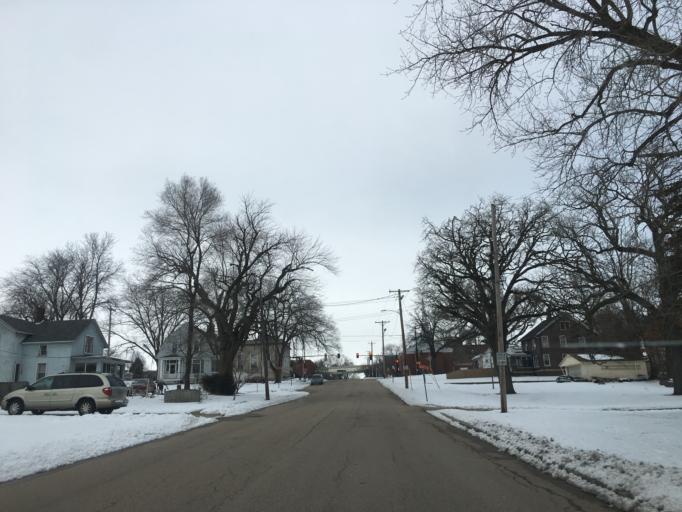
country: US
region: Illinois
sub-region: LaSalle County
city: Peru
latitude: 41.3261
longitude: -89.1251
